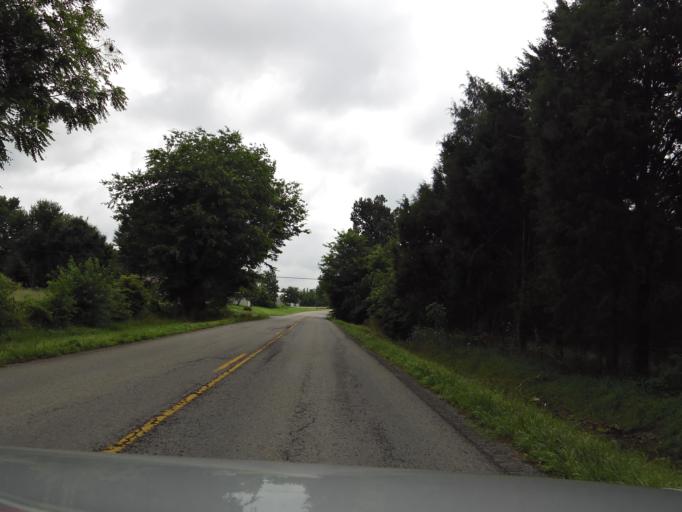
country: US
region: Kentucky
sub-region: Hopkins County
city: Madisonville
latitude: 37.3261
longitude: -87.3809
